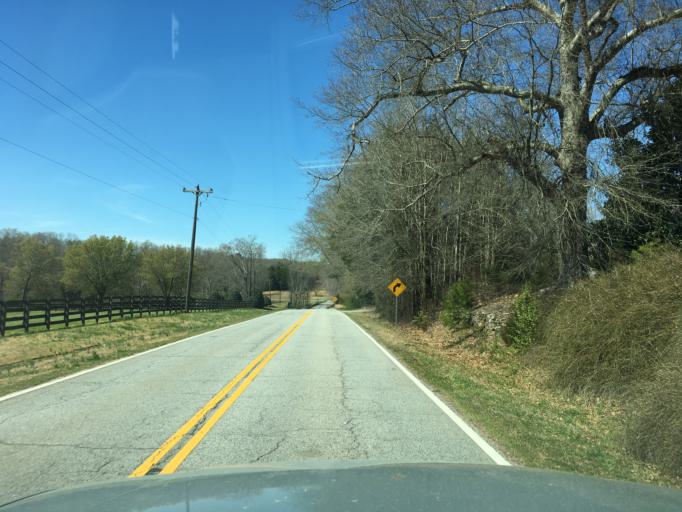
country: US
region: South Carolina
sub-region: Spartanburg County
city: Roebuck
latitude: 34.8782
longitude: -81.9944
